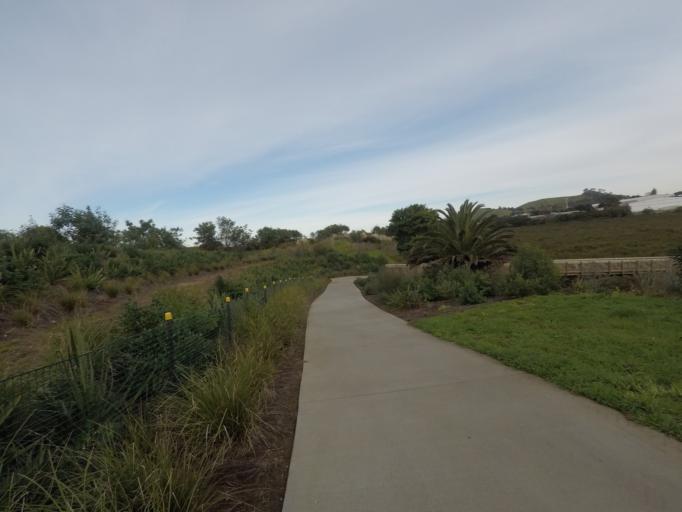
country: NZ
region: Auckland
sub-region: Auckland
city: Mangere
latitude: -36.9488
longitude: 174.8013
